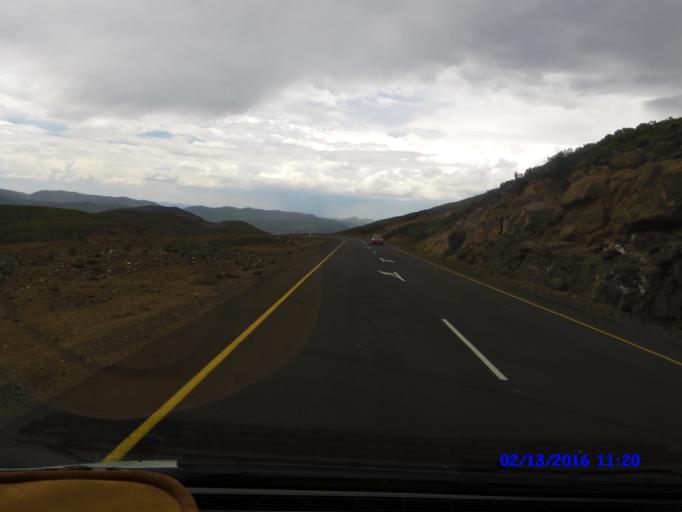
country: LS
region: Maseru
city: Nako
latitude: -29.7539
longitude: 27.9640
